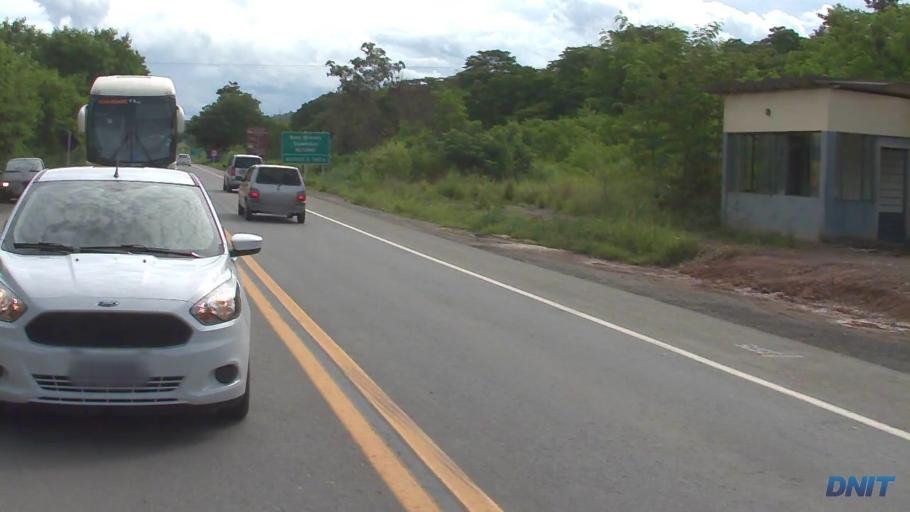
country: BR
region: Minas Gerais
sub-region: Ipaba
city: Ipaba
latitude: -19.3062
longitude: -42.3871
